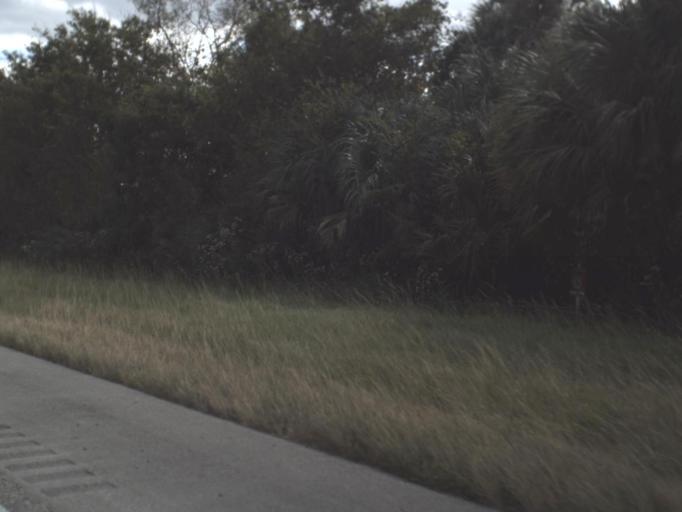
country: US
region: Florida
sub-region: Brevard County
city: Port Saint John
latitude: 28.4441
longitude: -80.8671
